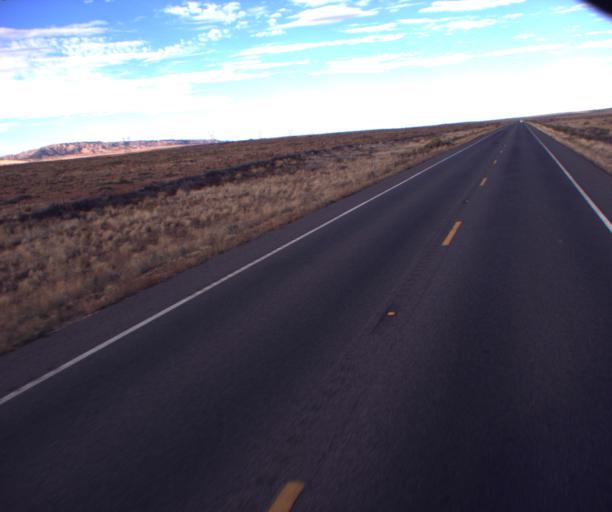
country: US
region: Arizona
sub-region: Apache County
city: Lukachukai
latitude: 36.9422
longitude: -109.2563
